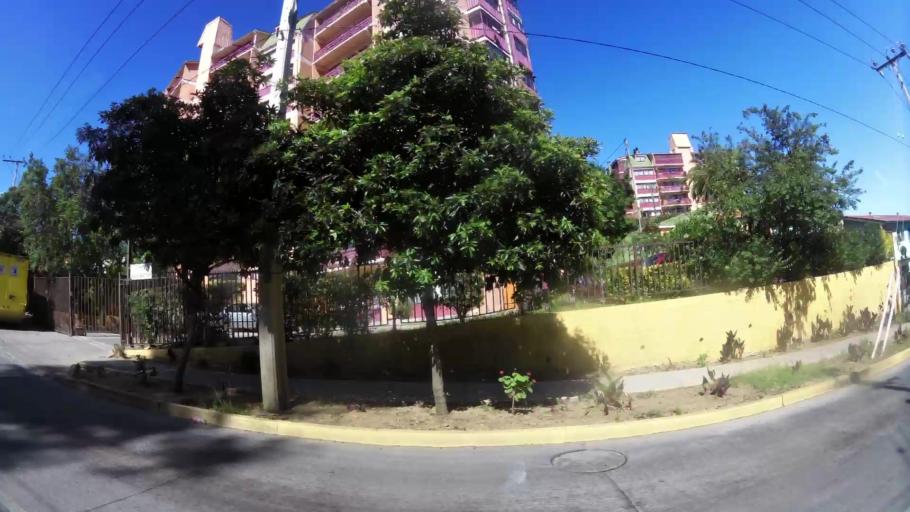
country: CL
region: Valparaiso
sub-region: Provincia de Valparaiso
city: Valparaiso
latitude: -33.0556
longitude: -71.5856
